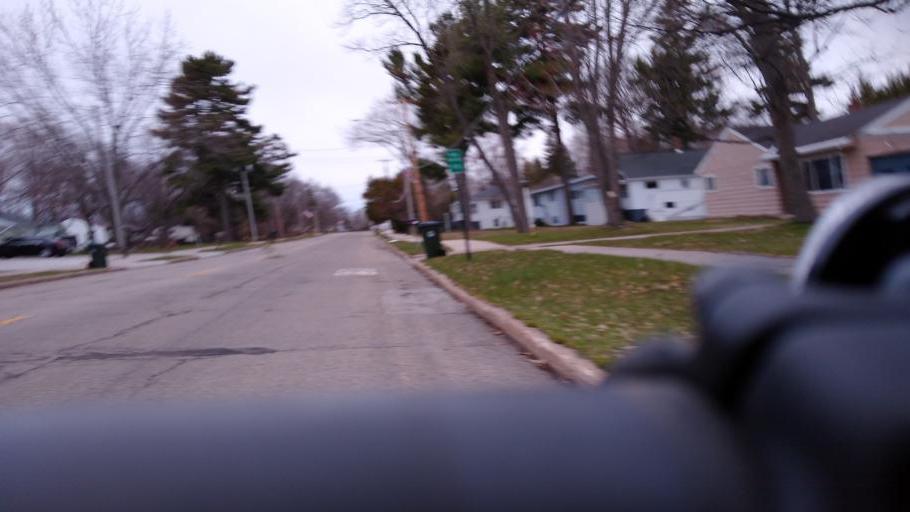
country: US
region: Michigan
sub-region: Delta County
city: Escanaba
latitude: 45.7173
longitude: -87.0749
